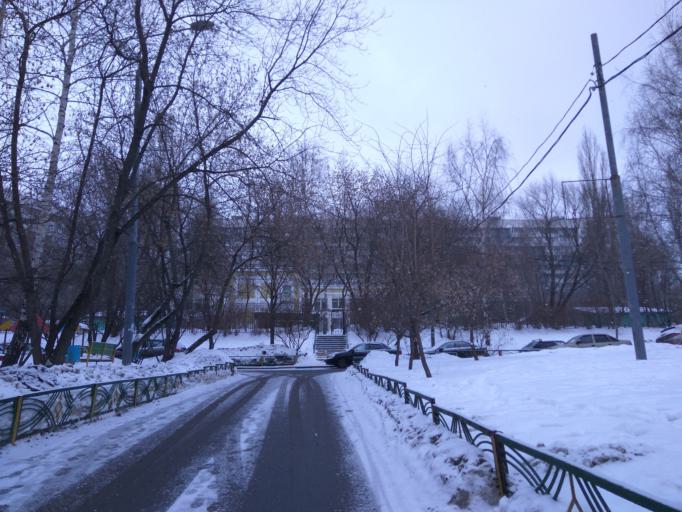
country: RU
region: Moscow
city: Strogino
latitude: 55.7948
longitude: 37.3977
